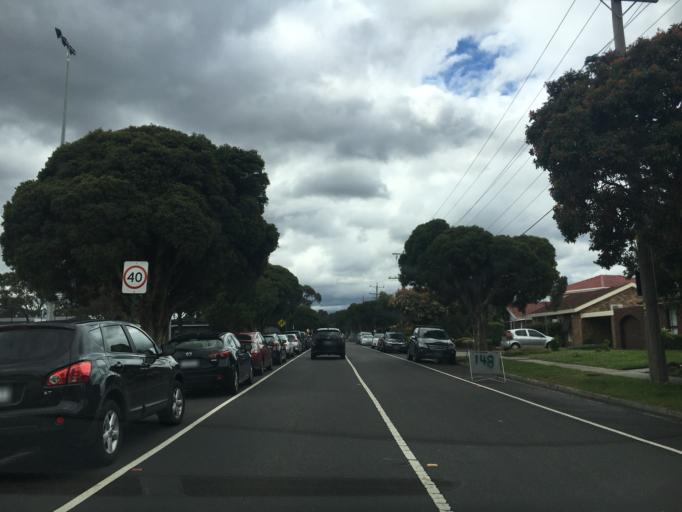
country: AU
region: Victoria
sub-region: Whitehorse
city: Vermont South
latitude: -37.8673
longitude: 145.1768
